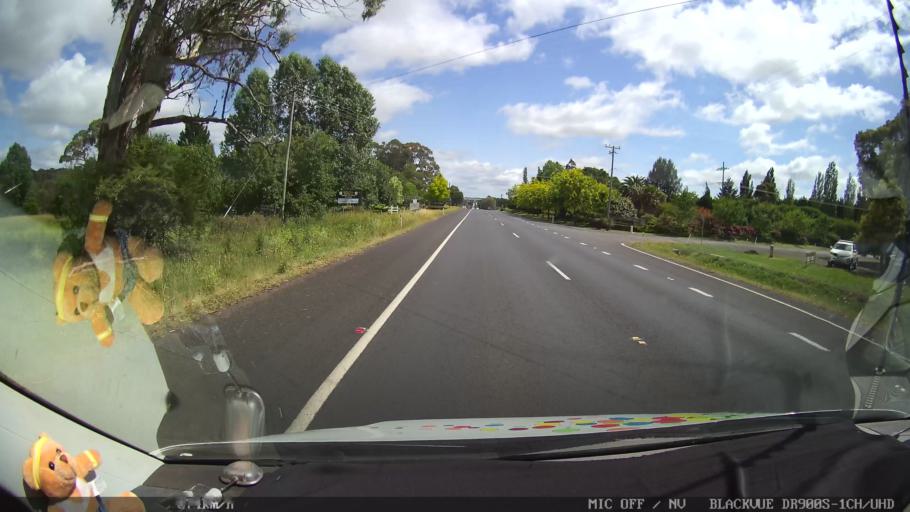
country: AU
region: New South Wales
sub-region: Glen Innes Severn
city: Glen Innes
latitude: -29.7614
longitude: 151.7338
